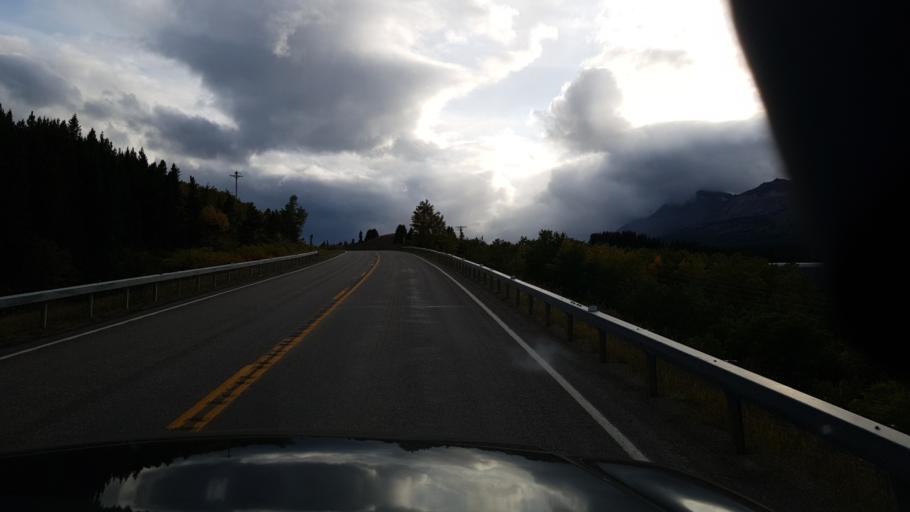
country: US
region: Montana
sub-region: Glacier County
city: South Browning
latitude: 48.3837
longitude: -113.2711
